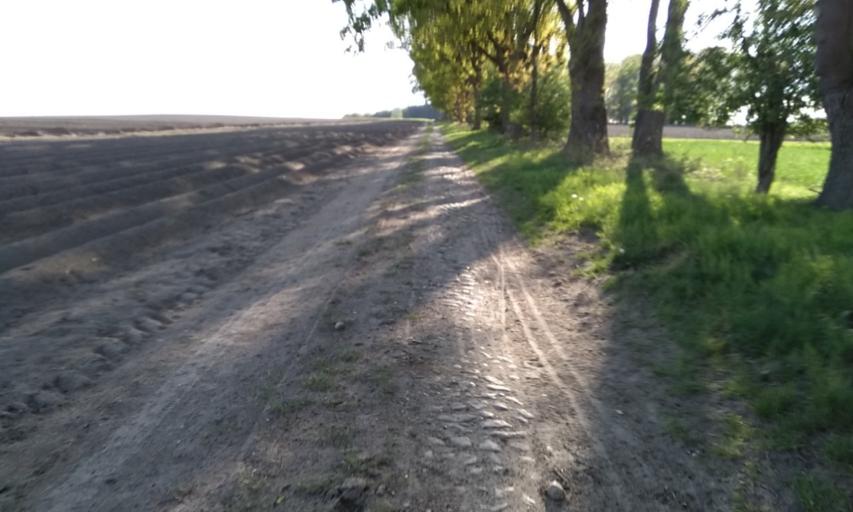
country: DE
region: Lower Saxony
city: Beckdorf
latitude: 53.4059
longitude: 9.5989
